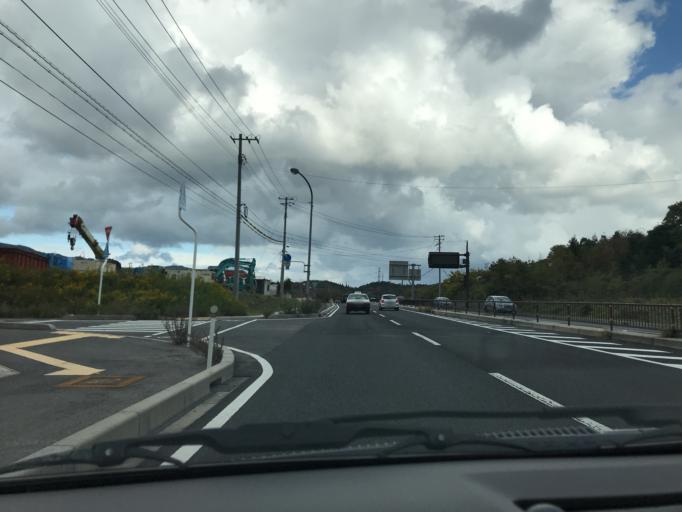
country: JP
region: Shimane
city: Matsue-shi
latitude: 35.4904
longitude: 133.0856
